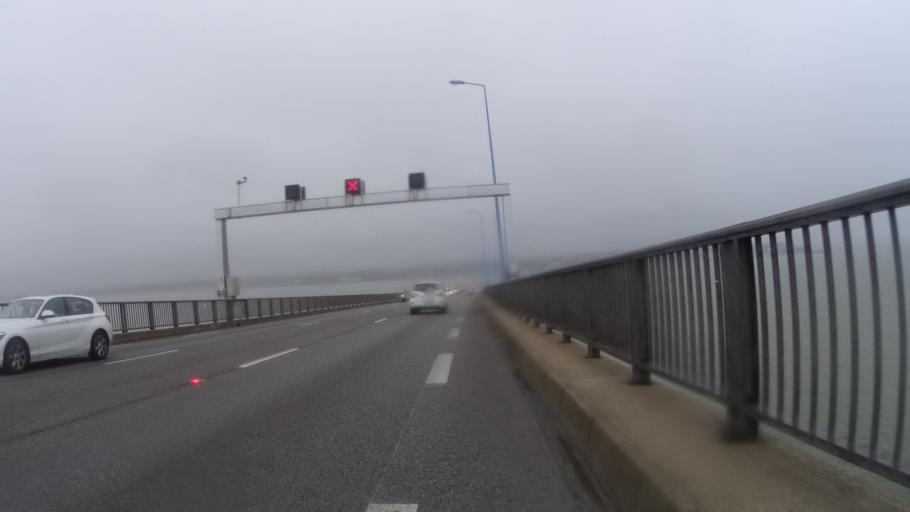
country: FR
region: Pays de la Loire
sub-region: Departement de la Loire-Atlantique
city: Saint-Brevin-les-Pins
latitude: 47.2797
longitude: -2.1665
